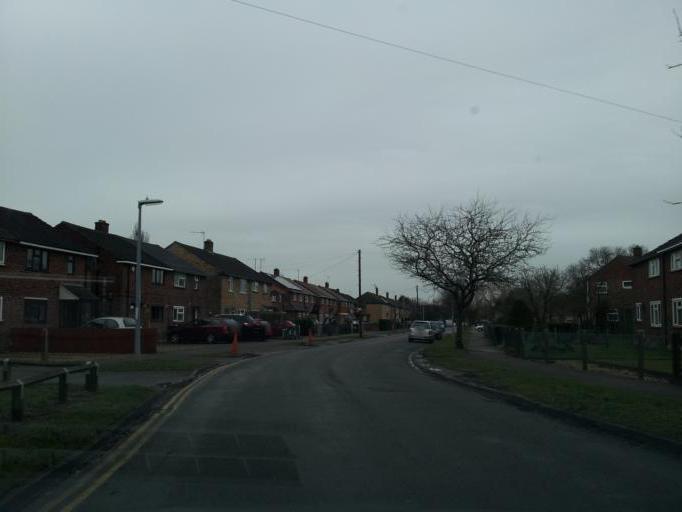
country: GB
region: England
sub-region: Cambridgeshire
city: Cambridge
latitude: 52.1836
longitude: 0.1535
